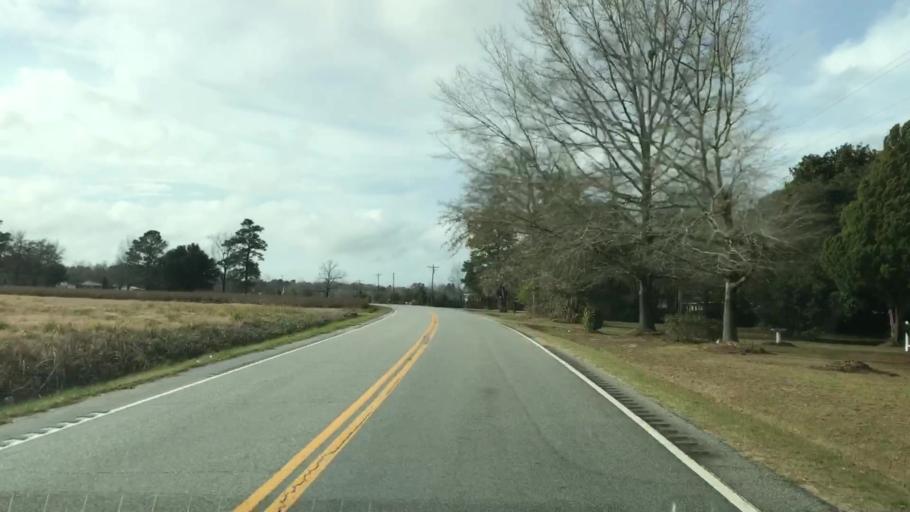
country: US
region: South Carolina
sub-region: Williamsburg County
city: Andrews
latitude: 33.5013
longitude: -79.5173
